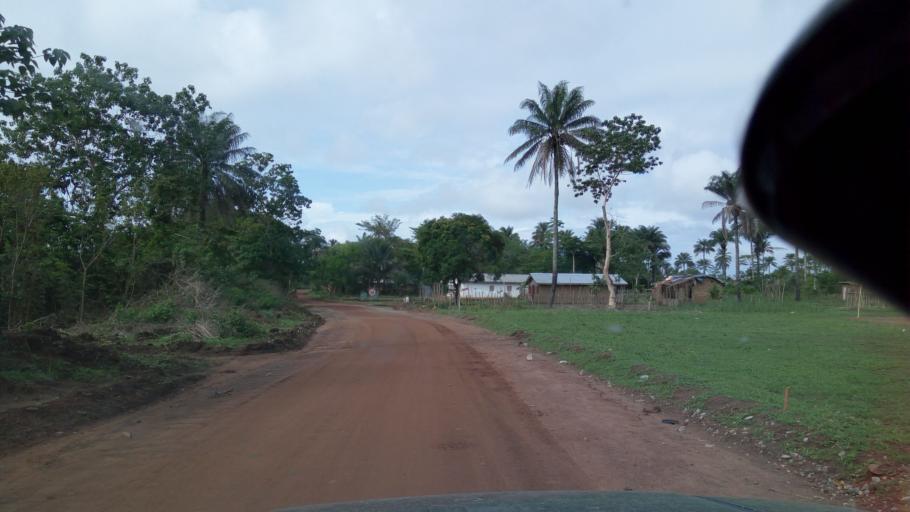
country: SL
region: Northern Province
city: Pepel
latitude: 8.6323
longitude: -13.0299
